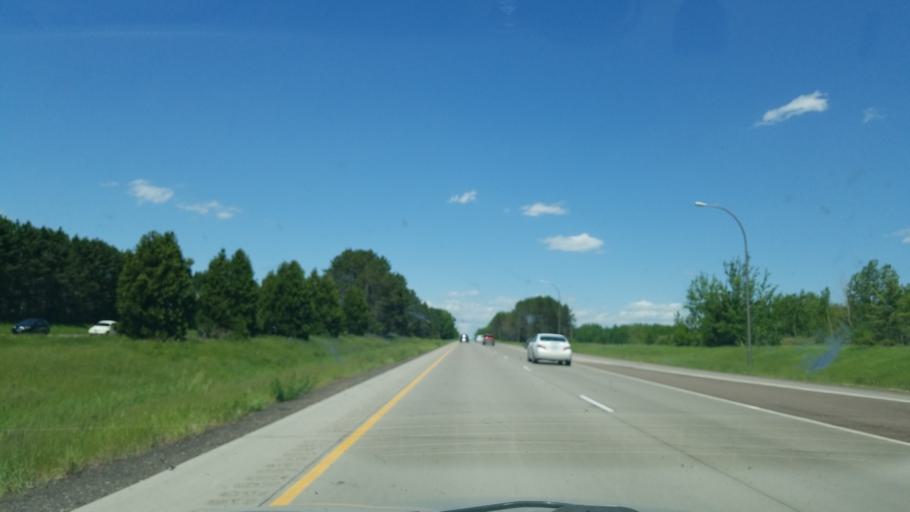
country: US
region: Minnesota
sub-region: Pine County
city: Sandstone
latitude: 46.1815
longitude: -92.8554
